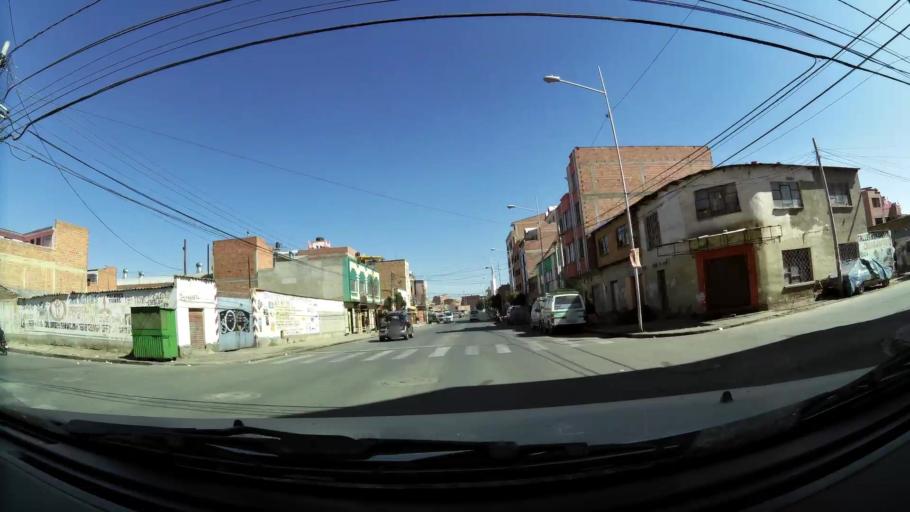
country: BO
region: La Paz
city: La Paz
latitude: -16.5167
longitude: -68.1532
